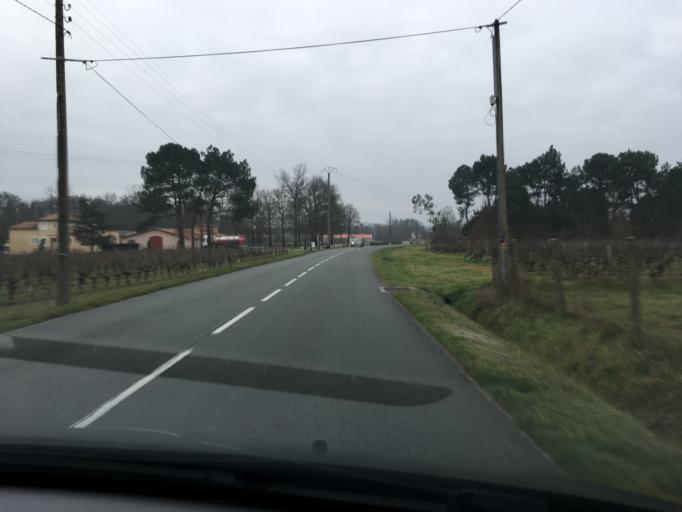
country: FR
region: Aquitaine
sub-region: Departement de la Gironde
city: Saint-Ciers-sur-Gironde
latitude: 45.2779
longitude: -0.5981
